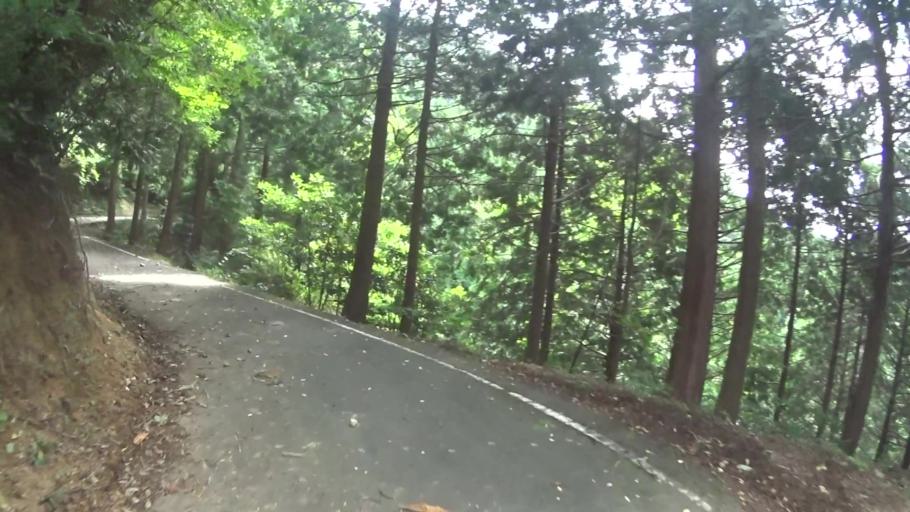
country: JP
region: Kyoto
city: Miyazu
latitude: 35.7359
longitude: 135.1957
